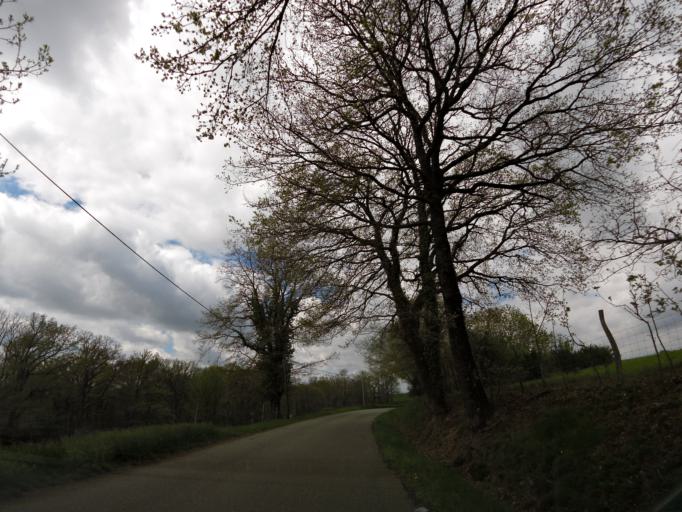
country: FR
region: Languedoc-Roussillon
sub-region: Departement de l'Aude
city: Villepinte
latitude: 43.3553
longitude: 2.1417
